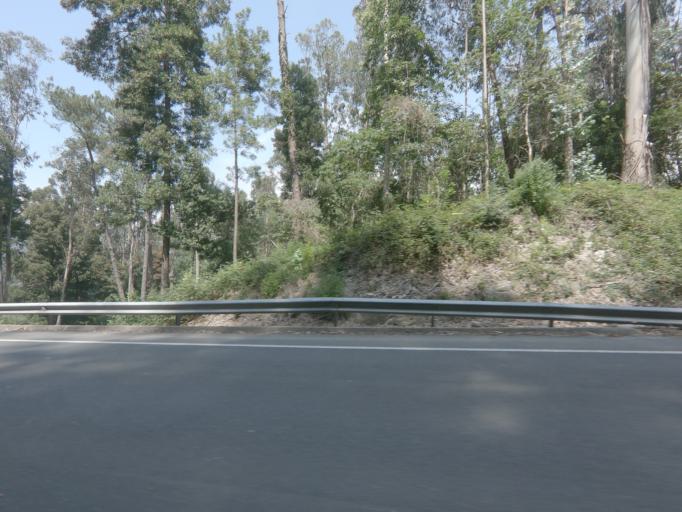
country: ES
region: Galicia
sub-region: Provincia de Pontevedra
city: Gondomar
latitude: 42.0913
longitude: -8.7529
